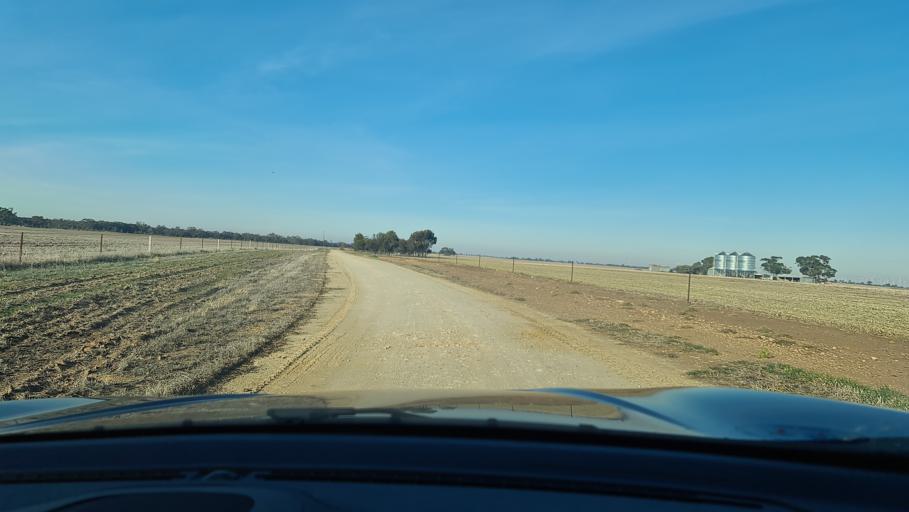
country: AU
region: Victoria
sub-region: Horsham
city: Horsham
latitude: -36.3619
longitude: 142.3958
